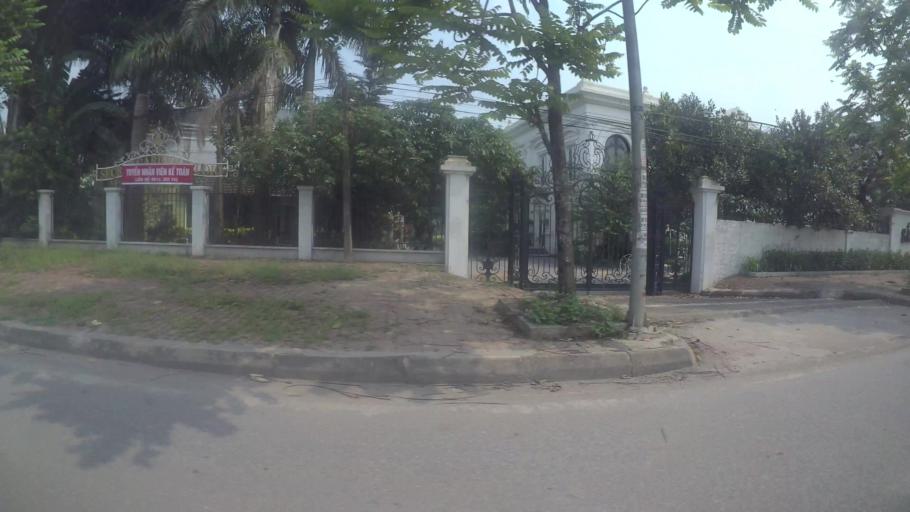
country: VN
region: Ha Noi
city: Quoc Oai
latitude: 21.0016
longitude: 105.6060
